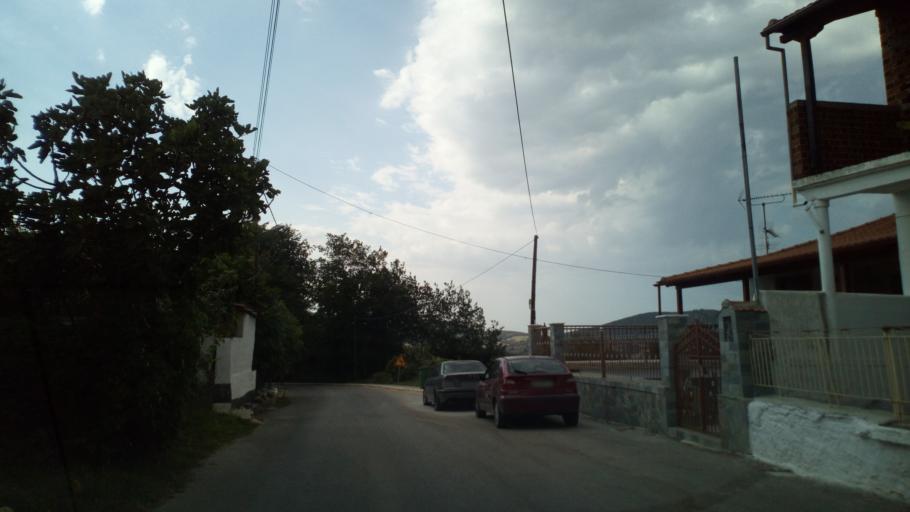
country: GR
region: Central Macedonia
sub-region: Nomos Chalkidikis
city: Galatista
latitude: 40.5136
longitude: 23.3494
